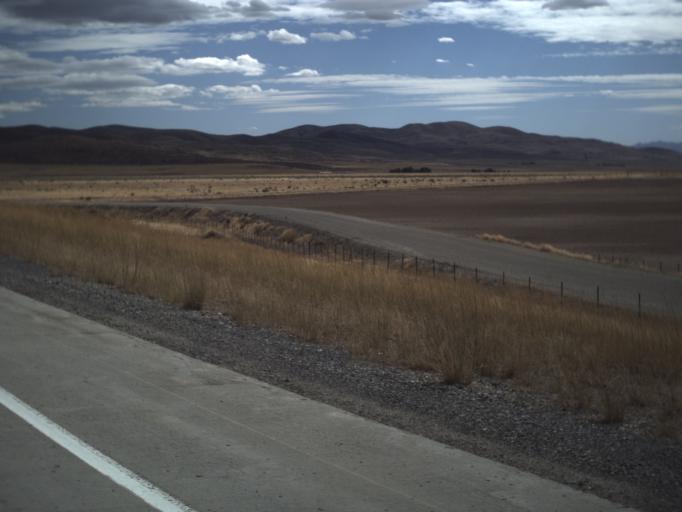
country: US
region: Utah
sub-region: Box Elder County
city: Garland
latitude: 41.8185
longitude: -112.4151
